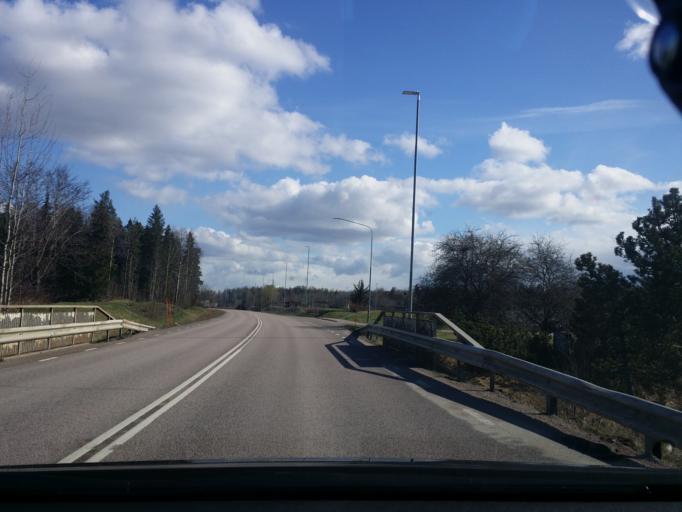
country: SE
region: Vaestmanland
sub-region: Sala Kommun
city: Sala
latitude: 59.9281
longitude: 16.5728
